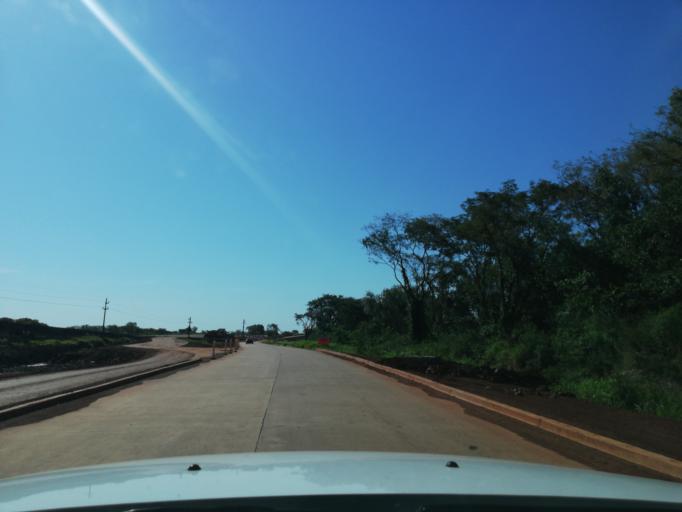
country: AR
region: Misiones
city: Santa Ana
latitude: -27.4151
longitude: -55.6111
